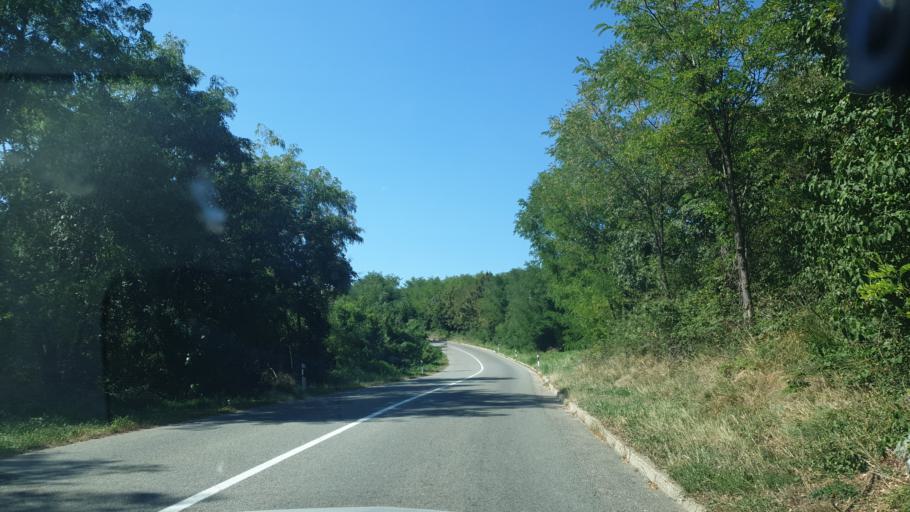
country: RS
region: Central Serbia
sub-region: Kolubarski Okrug
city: Mionica
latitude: 44.1742
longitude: 20.0076
